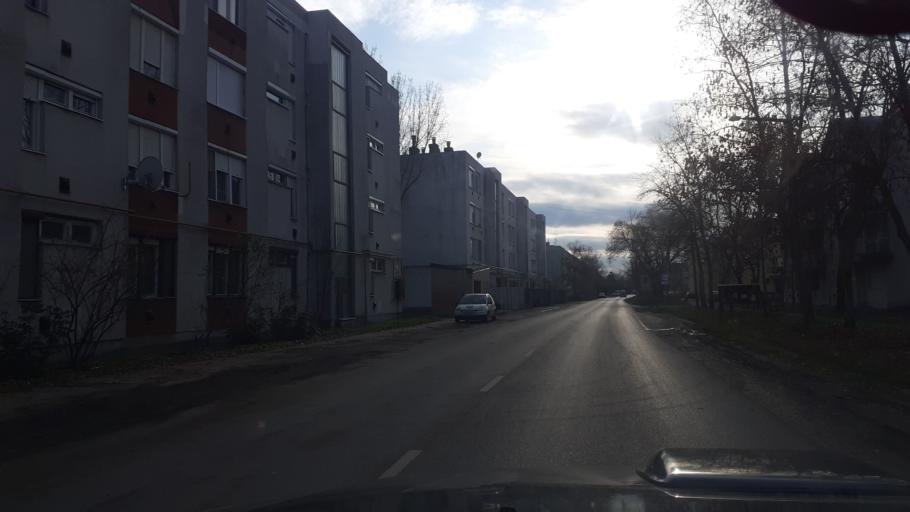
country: HU
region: Bacs-Kiskun
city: Kunszentmiklos
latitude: 47.0344
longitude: 19.1292
